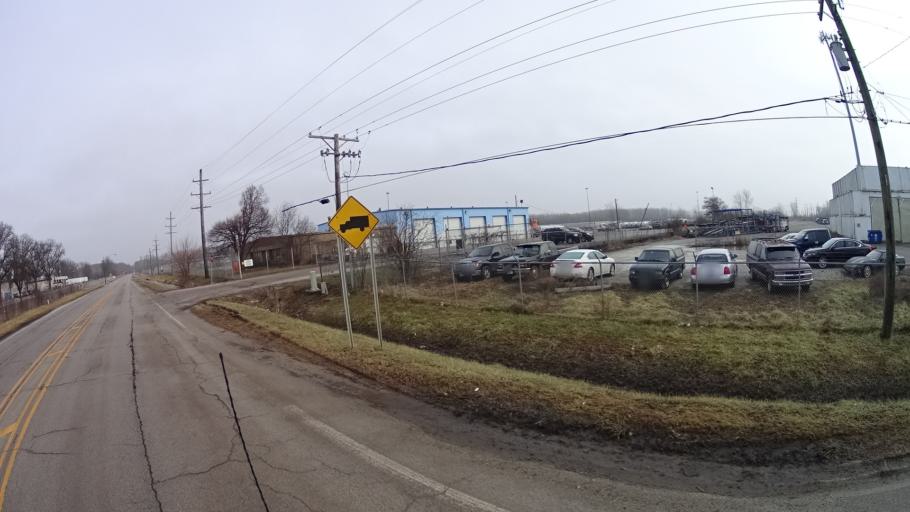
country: US
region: Illinois
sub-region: Cook County
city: Glenwood
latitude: 41.5248
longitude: -87.6164
